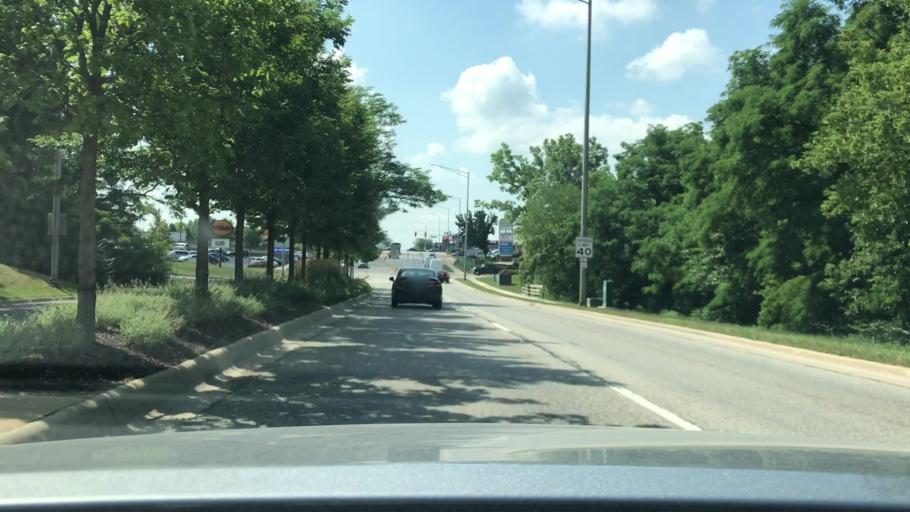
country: US
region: Illinois
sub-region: Will County
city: Bolingbrook
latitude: 41.7135
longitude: -88.0689
